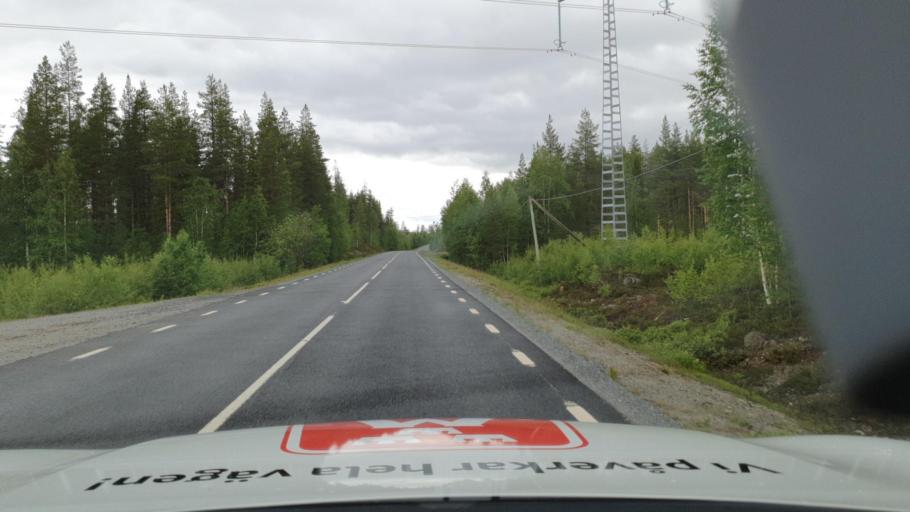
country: SE
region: Vaesterbotten
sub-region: Dorotea Kommun
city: Dorotea
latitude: 64.2004
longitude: 16.5709
